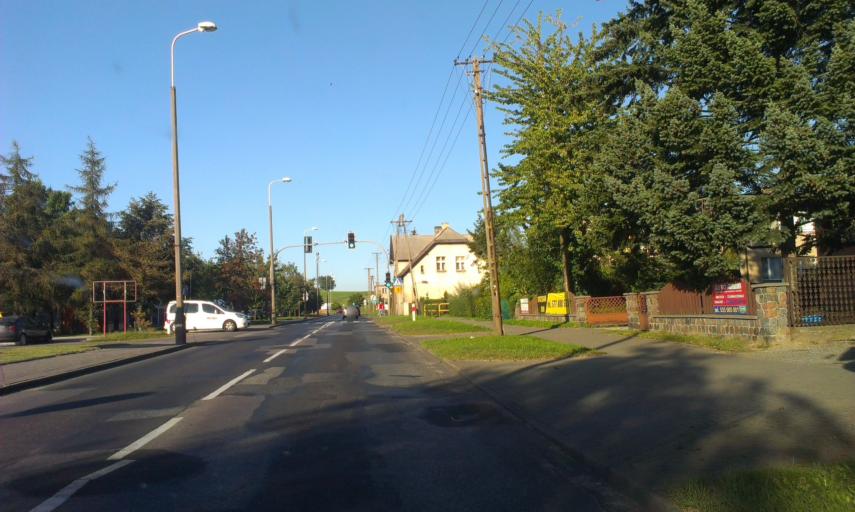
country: PL
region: Kujawsko-Pomorskie
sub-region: Powiat tucholski
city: Tuchola
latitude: 53.5834
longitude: 17.8738
